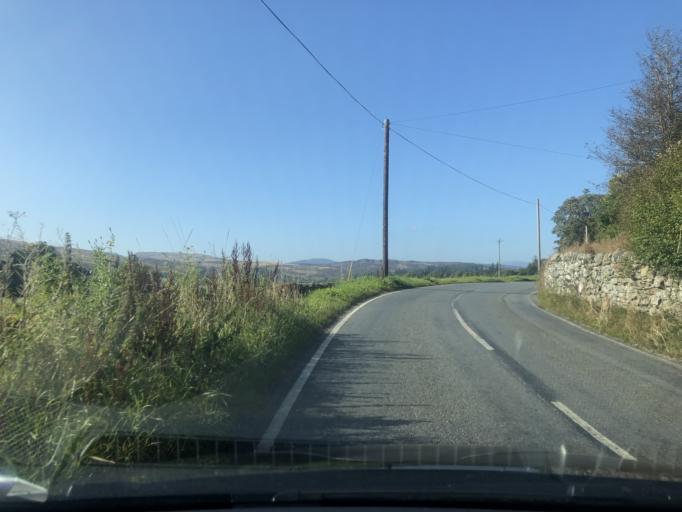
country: GB
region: Scotland
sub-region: Perth and Kinross
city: Blairgowrie
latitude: 56.6827
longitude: -3.4719
